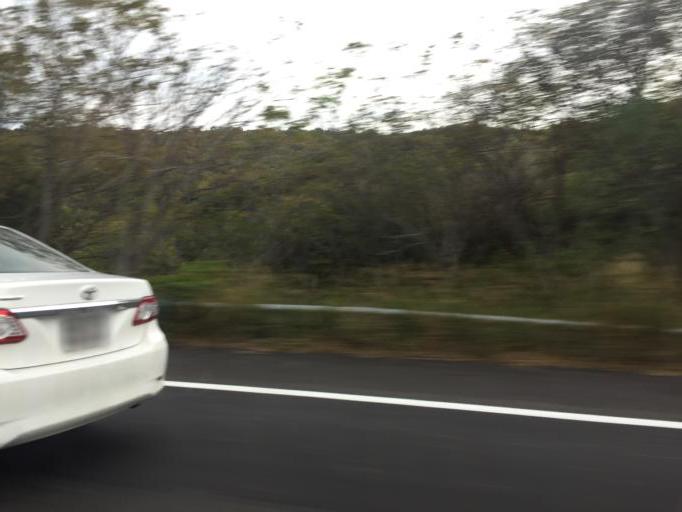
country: MX
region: Michoacan
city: Copandaro de Galeana
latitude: 19.8875
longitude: -101.2303
